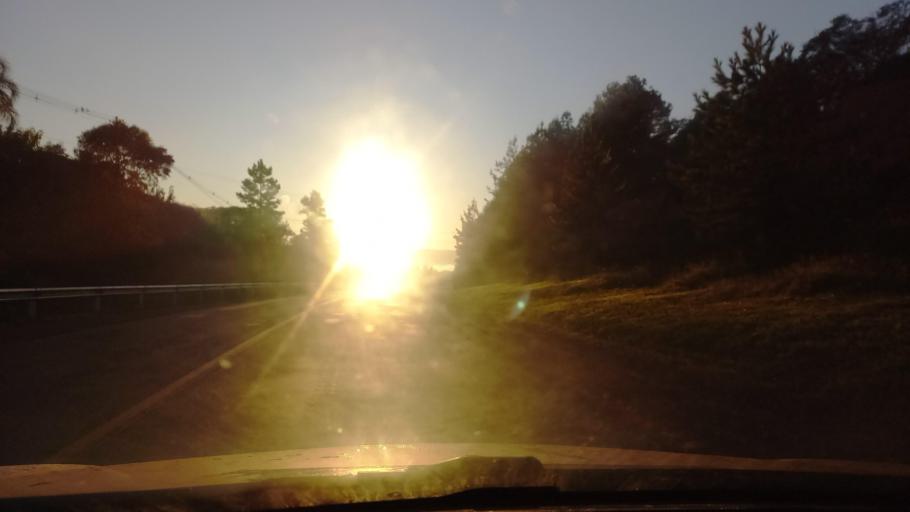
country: BR
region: Rio Grande do Sul
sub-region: Candelaria
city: Candelaria
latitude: -29.6814
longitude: -52.8415
